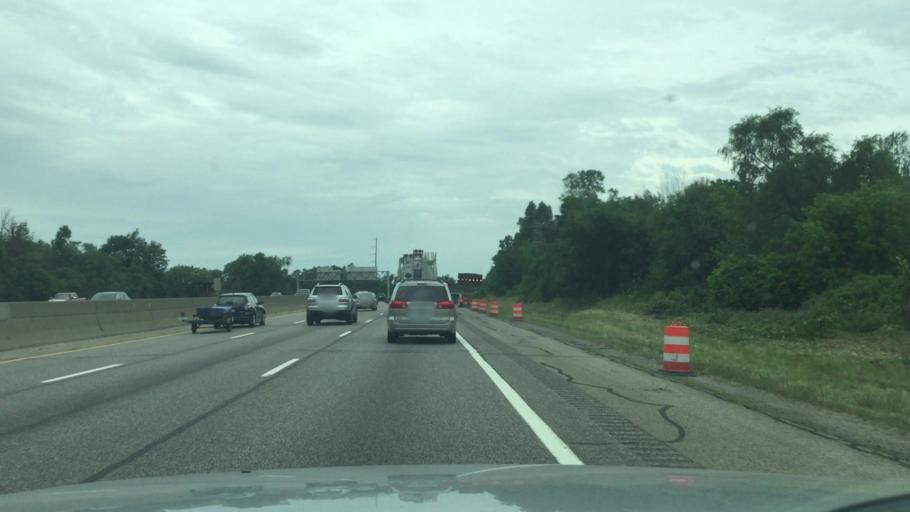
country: US
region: Michigan
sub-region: Genesee County
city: Flint
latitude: 42.9930
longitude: -83.7440
